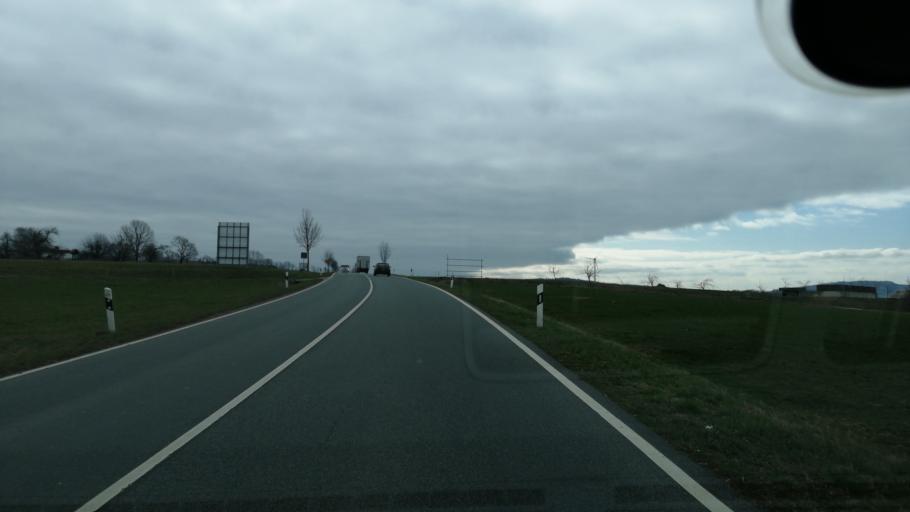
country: DE
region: Saxony
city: Lobau
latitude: 51.0814
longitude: 14.6735
